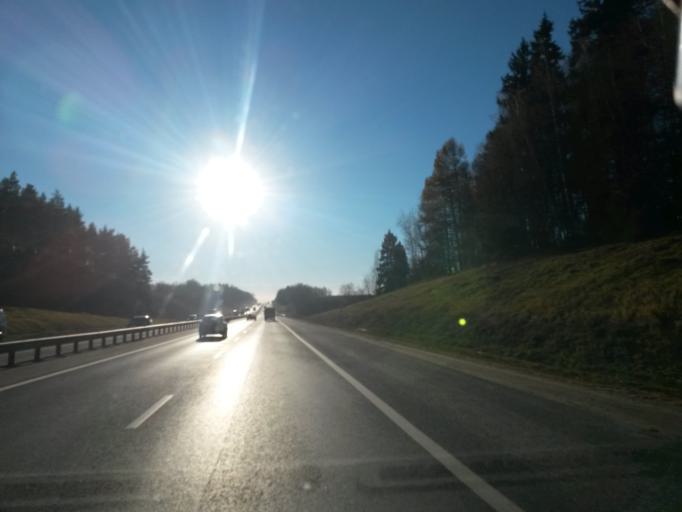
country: RU
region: Moskovskaya
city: Ashukino
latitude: 56.1259
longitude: 37.9866
